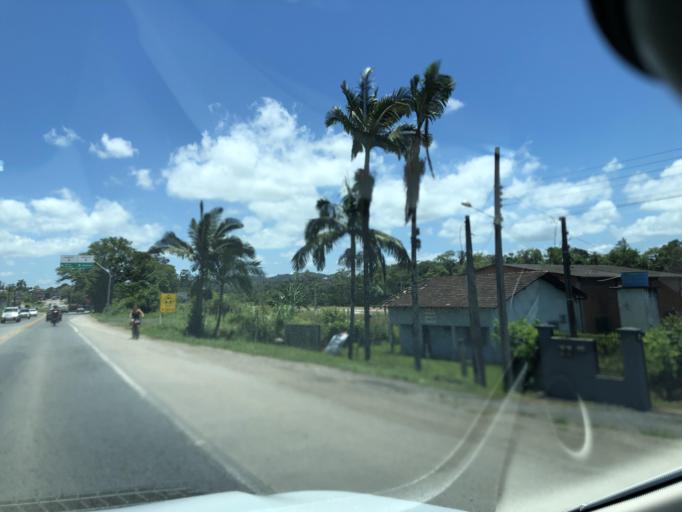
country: BR
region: Santa Catarina
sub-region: Joinville
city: Joinville
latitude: -26.4175
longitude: -48.7760
